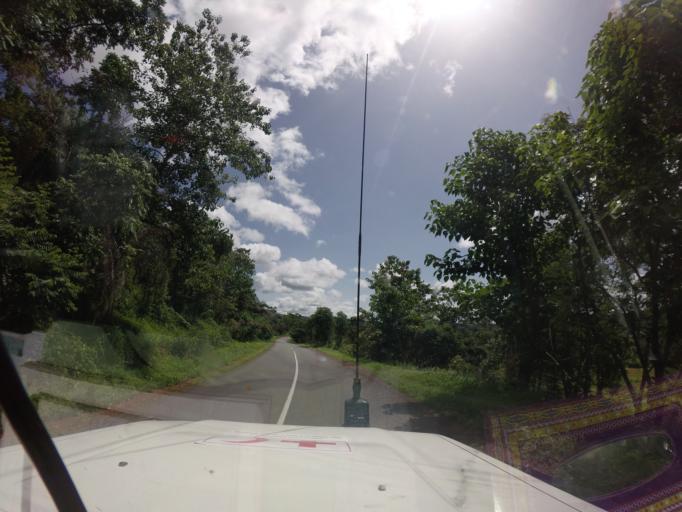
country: GN
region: Mamou
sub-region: Mamou Prefecture
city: Mamou
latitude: 10.1782
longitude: -11.8098
